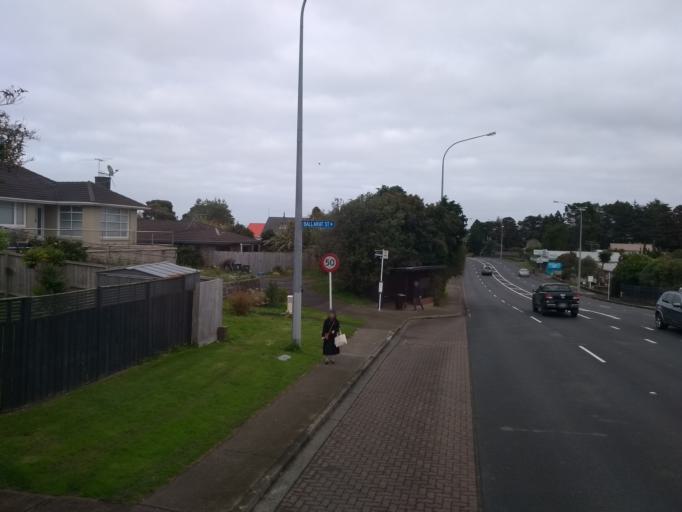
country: NZ
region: Auckland
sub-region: Auckland
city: Tamaki
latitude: -36.8984
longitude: 174.8227
